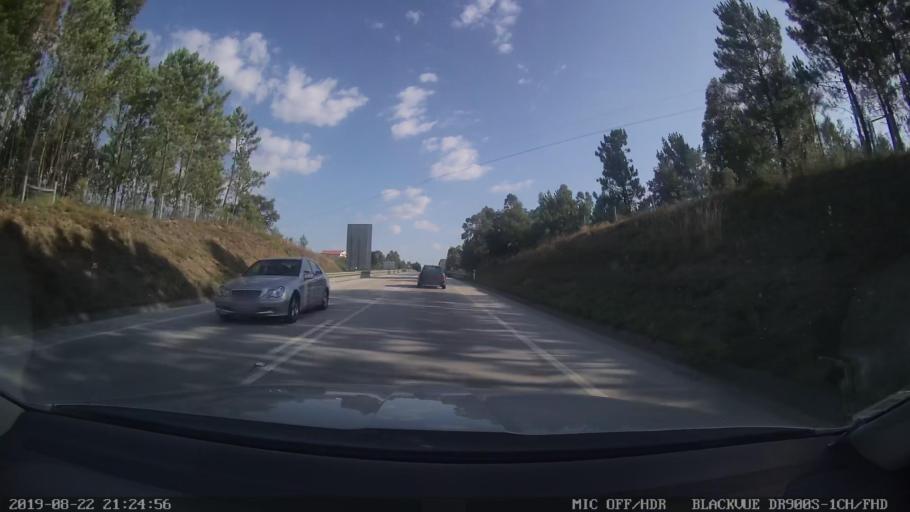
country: PT
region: Castelo Branco
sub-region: Serta
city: Serta
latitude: 39.8474
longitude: -8.1242
